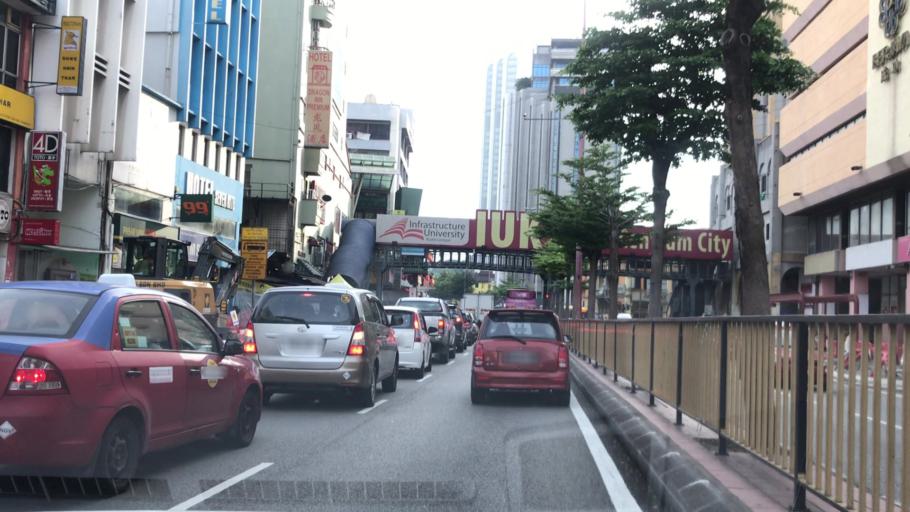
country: MY
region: Kuala Lumpur
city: Kuala Lumpur
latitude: 3.1454
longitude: 101.6982
